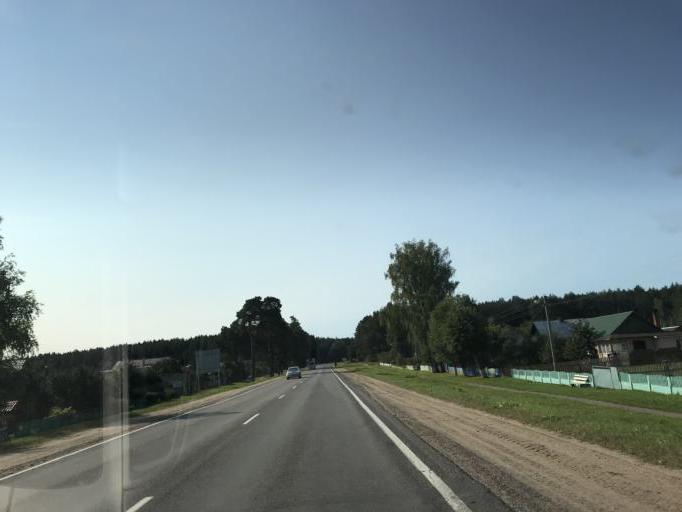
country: BY
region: Mogilev
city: Buynichy
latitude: 53.8207
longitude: 30.2393
